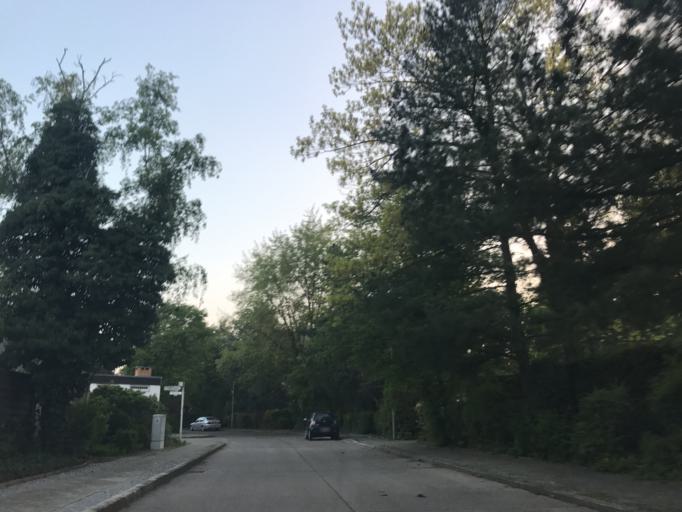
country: DE
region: Berlin
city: Wilhelmstadt
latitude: 52.5171
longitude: 13.1660
